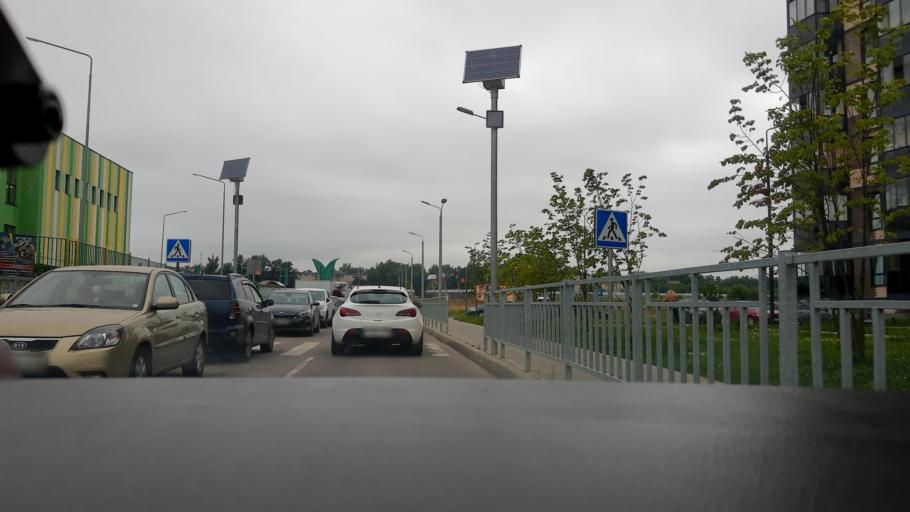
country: RU
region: Moskovskaya
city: Aprelevka
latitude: 55.5317
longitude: 37.0613
